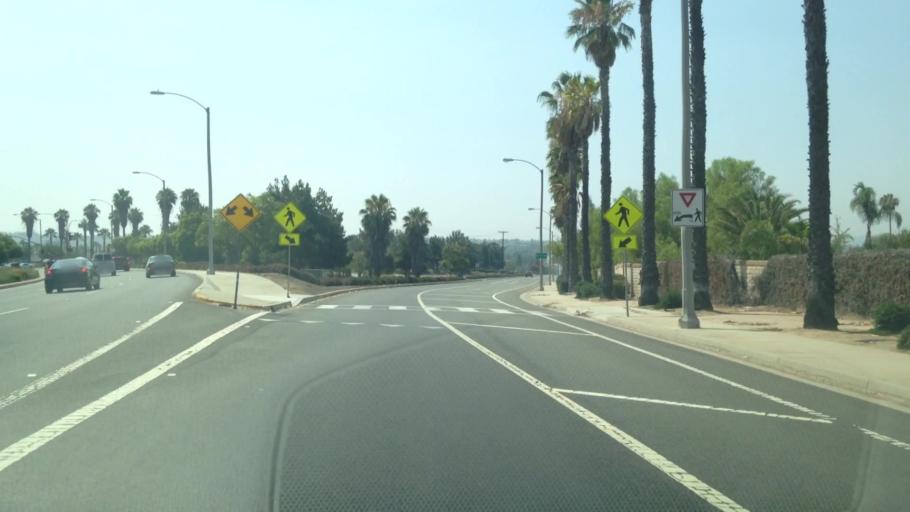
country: US
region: California
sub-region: Riverside County
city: Woodcrest
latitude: 33.9183
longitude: -117.3323
